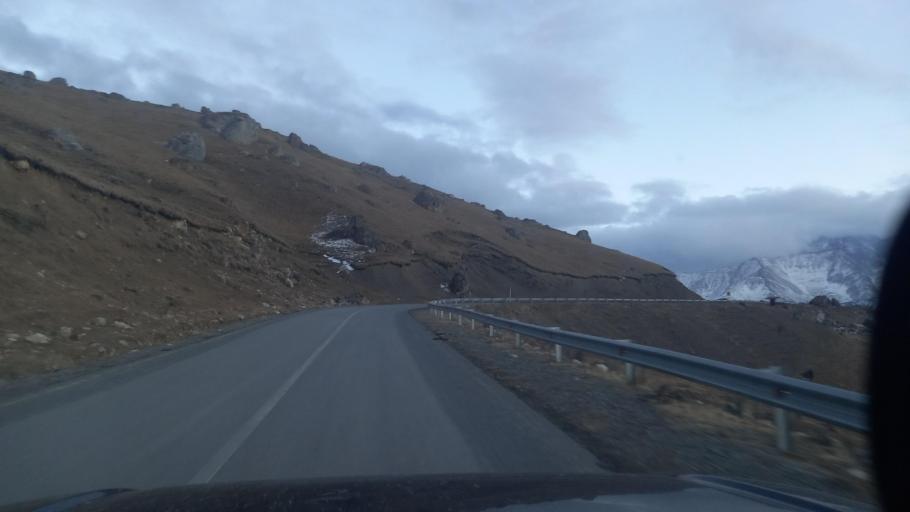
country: RU
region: Ingushetiya
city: Dzhayrakh
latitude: 42.8221
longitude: 44.8296
